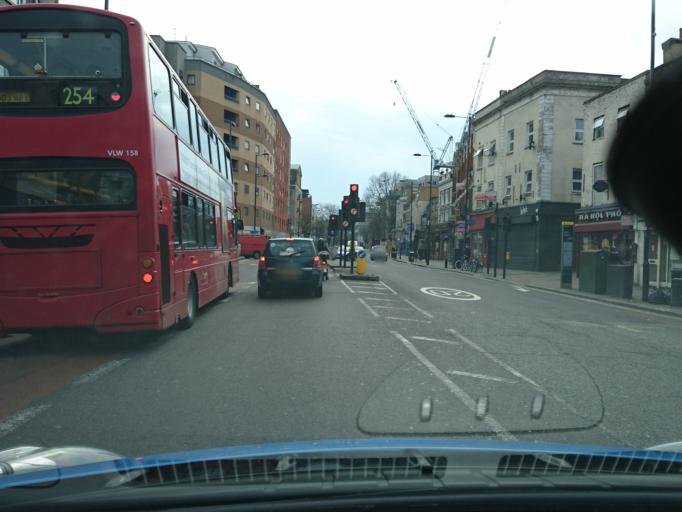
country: GB
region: England
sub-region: Greater London
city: Hackney
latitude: 51.5404
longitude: -0.0554
